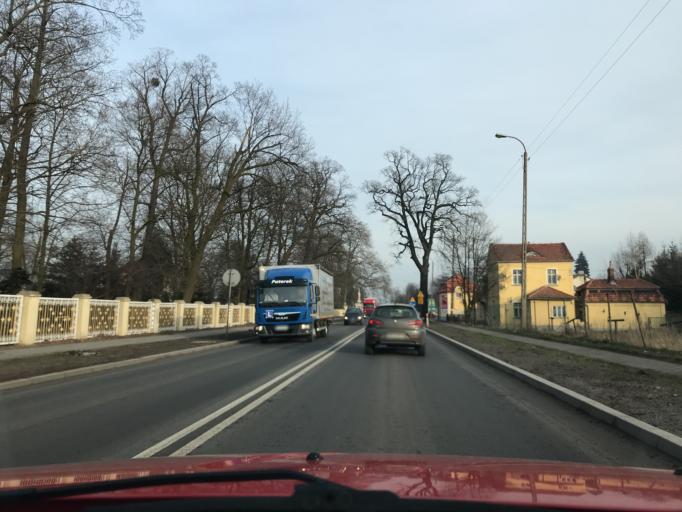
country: PL
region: Greater Poland Voivodeship
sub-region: Powiat jarocinski
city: Witaszyce
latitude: 51.9417
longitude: 17.5598
